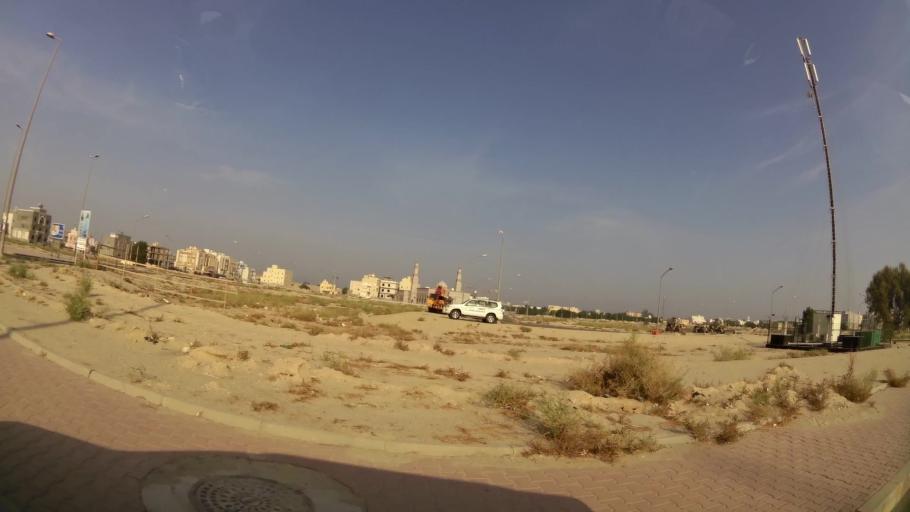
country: KW
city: Al Funaytis
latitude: 29.2077
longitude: 48.0991
